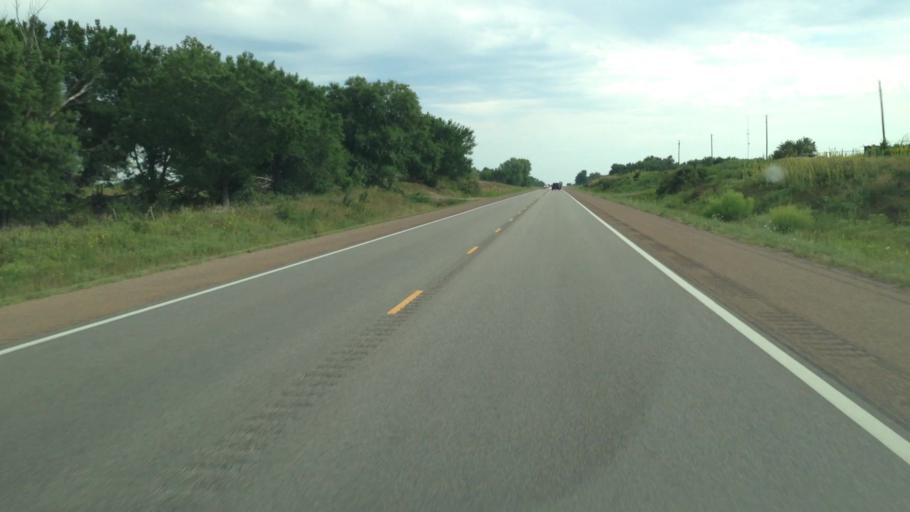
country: US
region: Kansas
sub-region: Woodson County
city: Yates Center
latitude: 37.9941
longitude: -95.7388
